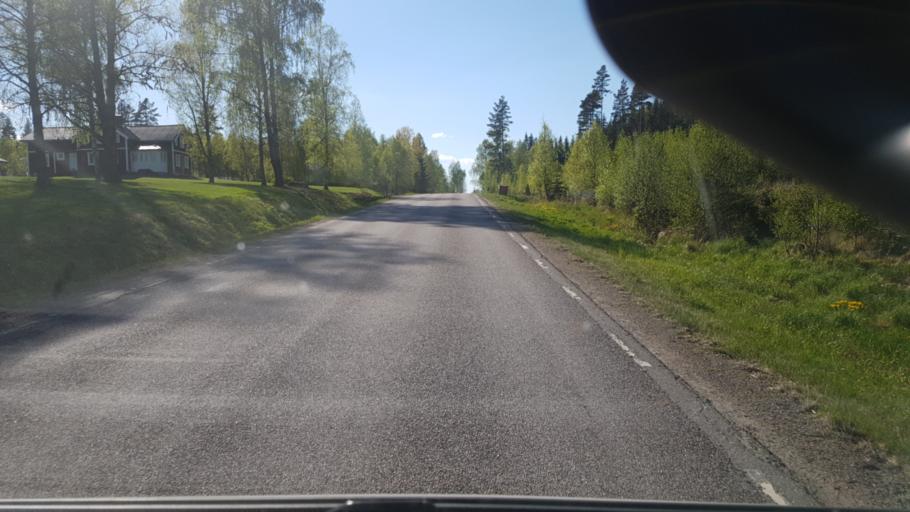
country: SE
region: Vaermland
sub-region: Eda Kommun
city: Charlottenberg
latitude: 59.8707
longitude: 12.4094
